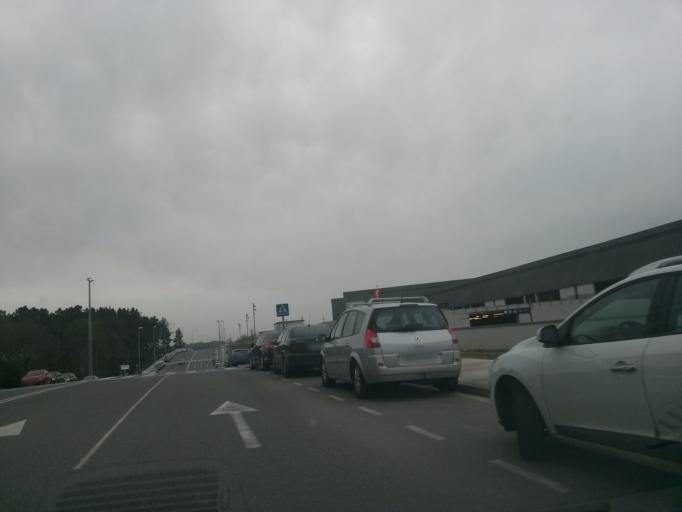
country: ES
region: Galicia
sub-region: Provincia de Lugo
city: Lugo
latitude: 43.0200
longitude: -7.5369
